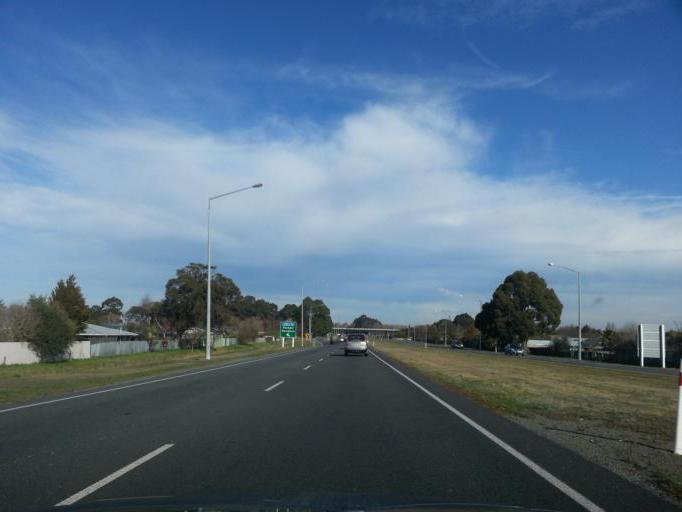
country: NZ
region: Canterbury
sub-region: Waimakariri District
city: Kaiapoi
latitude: -43.3822
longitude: 172.6432
